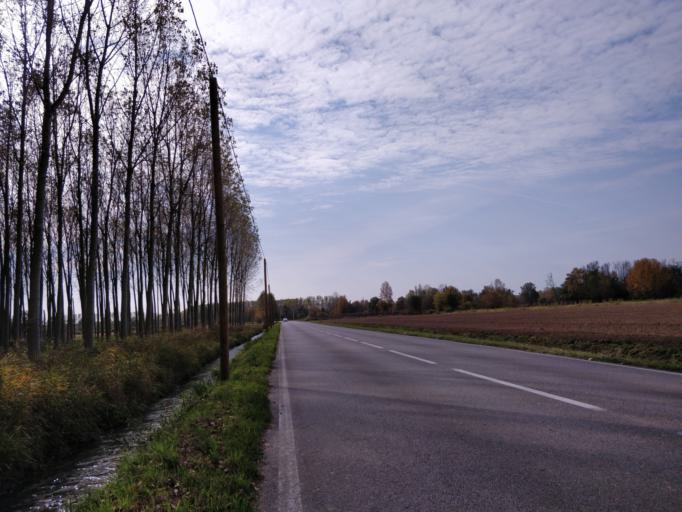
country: IT
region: Friuli Venezia Giulia
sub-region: Provincia di Udine
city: Bertiolo
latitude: 45.9315
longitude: 13.0501
